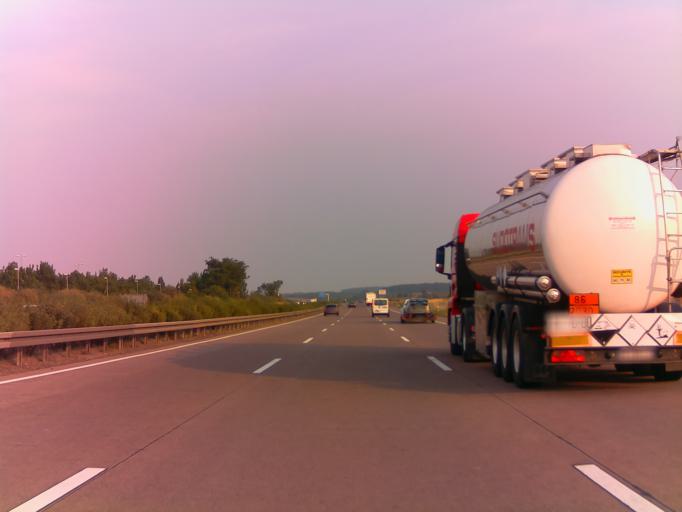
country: DE
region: Thuringia
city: Horselgau
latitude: 50.9139
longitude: 10.5835
